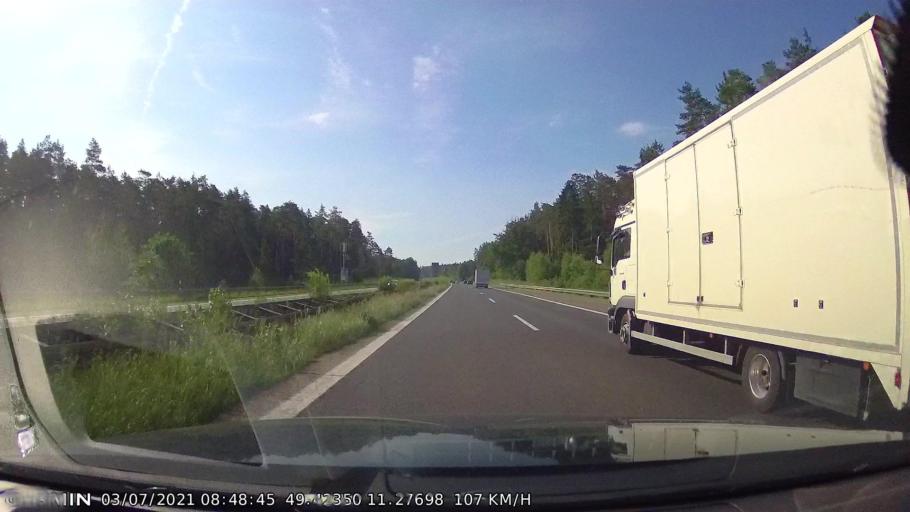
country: DE
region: Bavaria
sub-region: Regierungsbezirk Mittelfranken
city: Leinburg
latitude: 49.4235
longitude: 11.2770
